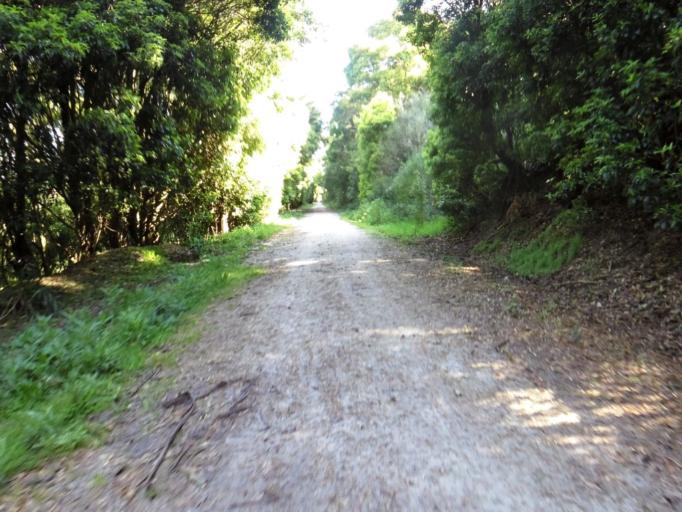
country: AU
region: Victoria
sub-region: Latrobe
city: Morwell
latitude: -38.6787
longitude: 146.1597
